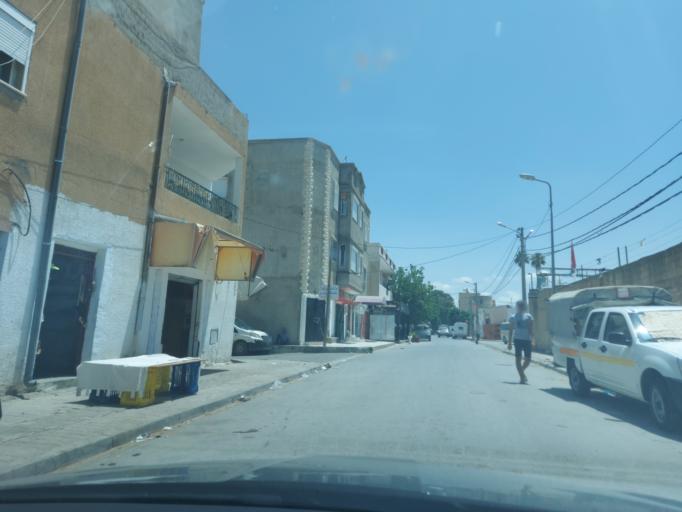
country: TN
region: Silyanah
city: Siliana
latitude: 36.0881
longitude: 9.3675
